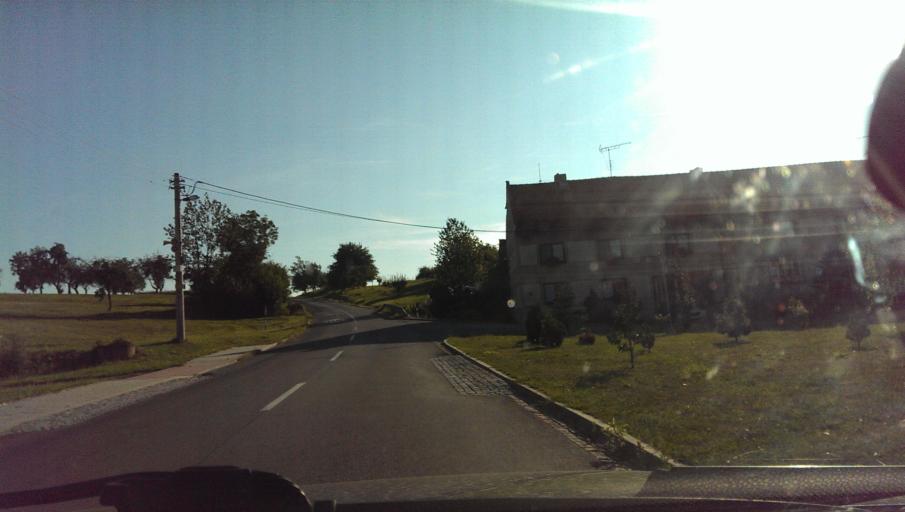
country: CZ
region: Zlin
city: Chvalcov
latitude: 49.4691
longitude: 17.7161
